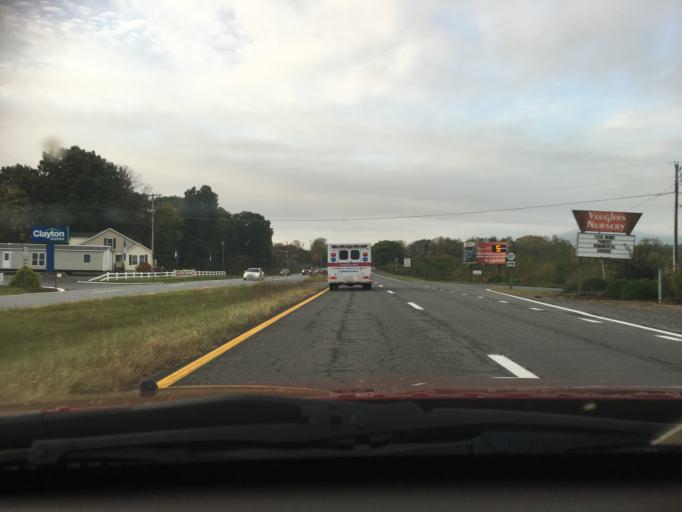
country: US
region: Virginia
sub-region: Pulaski County
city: Dublin
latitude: 37.0899
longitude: -80.6883
